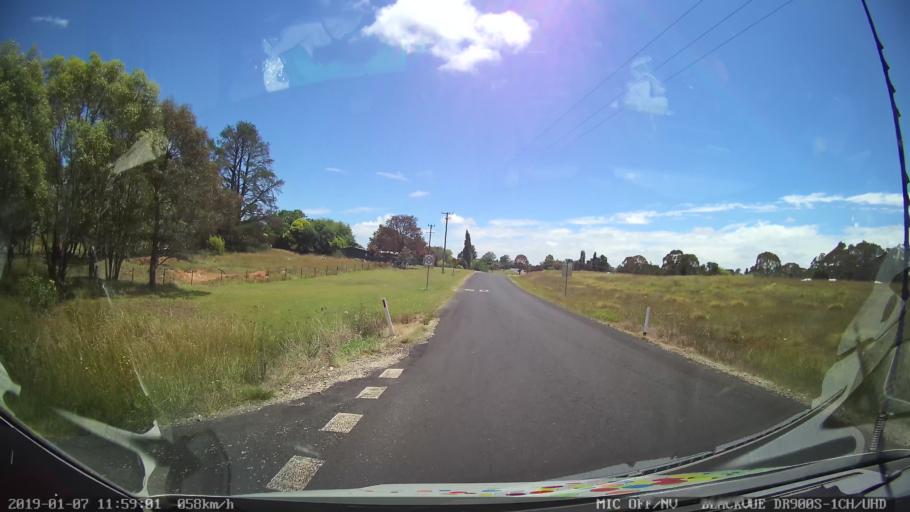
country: AU
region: New South Wales
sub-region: Guyra
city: Guyra
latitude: -30.2470
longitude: 151.6690
